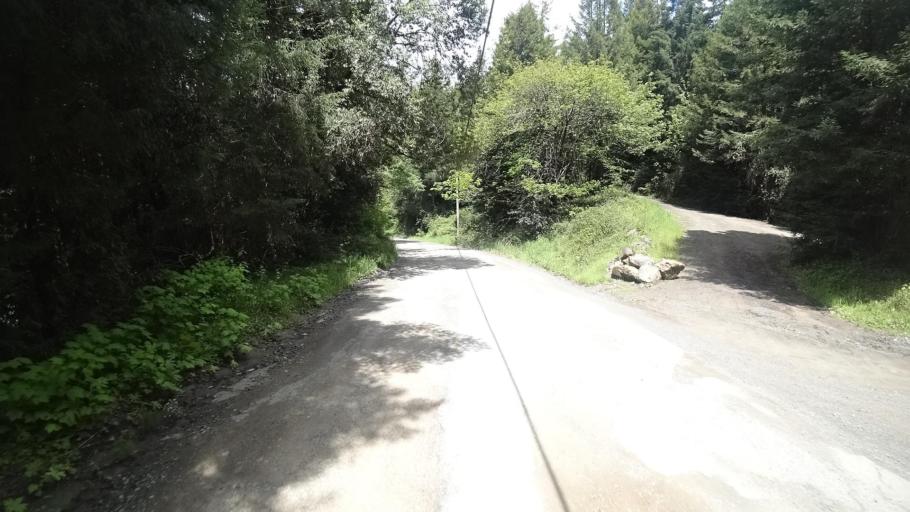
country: US
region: California
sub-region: Humboldt County
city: Blue Lake
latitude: 40.8448
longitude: -123.8935
